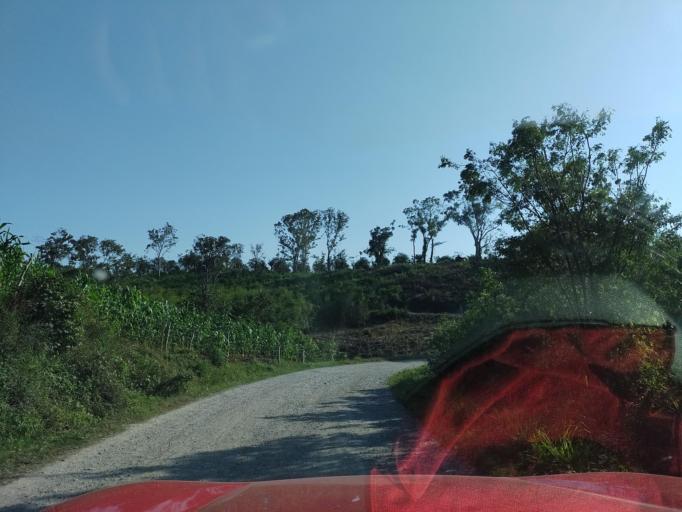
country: MX
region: Veracruz
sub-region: Papantla
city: Polutla
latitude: 20.4531
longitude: -97.2399
